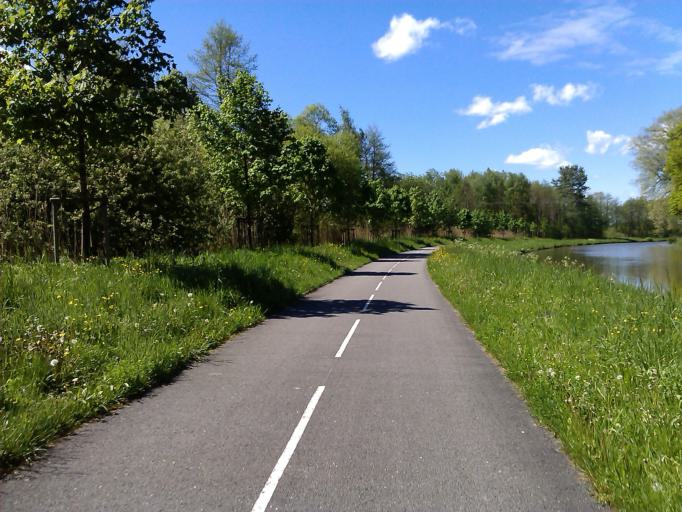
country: FR
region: Franche-Comte
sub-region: Territoire de Belfort
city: Montreux-Chateau
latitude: 47.5967
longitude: 6.9942
